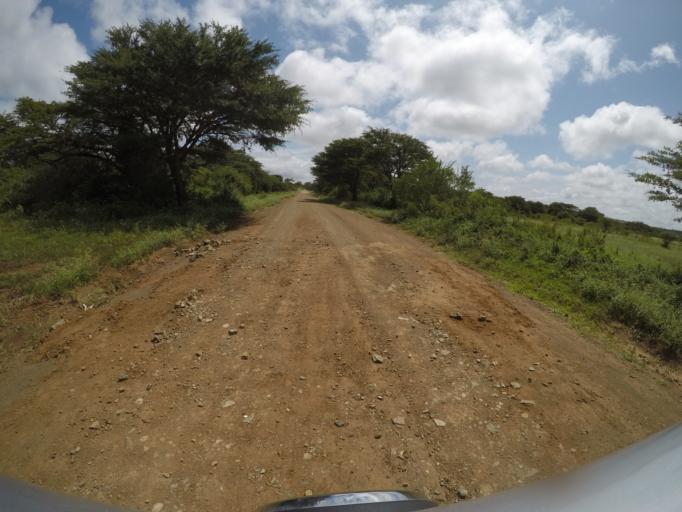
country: ZA
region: KwaZulu-Natal
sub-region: uThungulu District Municipality
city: Empangeni
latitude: -28.5702
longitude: 31.8368
